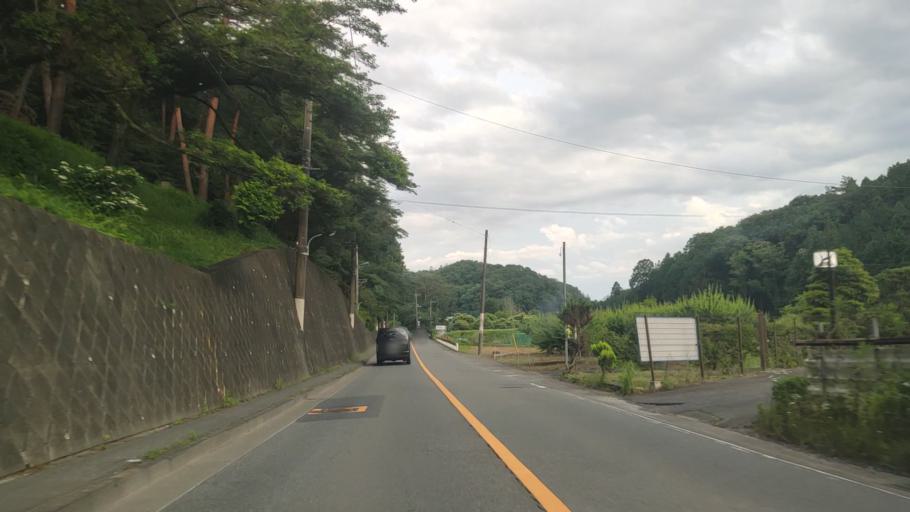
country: JP
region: Saitama
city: Hanno
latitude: 35.8184
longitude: 139.2953
